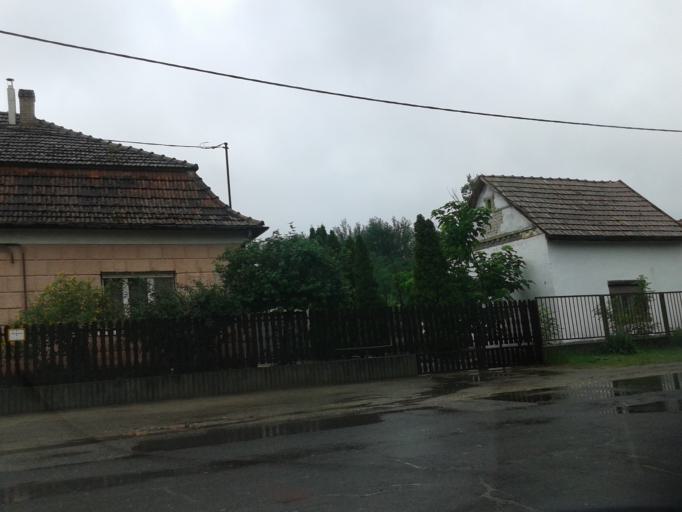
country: HU
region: Bacs-Kiskun
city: Kelebia
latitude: 46.2557
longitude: 19.6577
